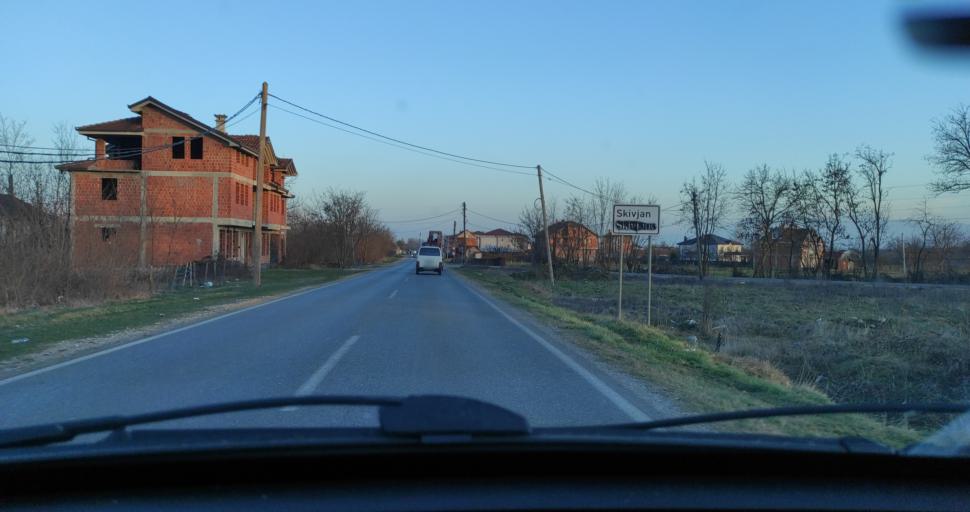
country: XK
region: Gjakova
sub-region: Komuna e Decanit
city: Gllogjan
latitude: 42.4363
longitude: 20.3729
